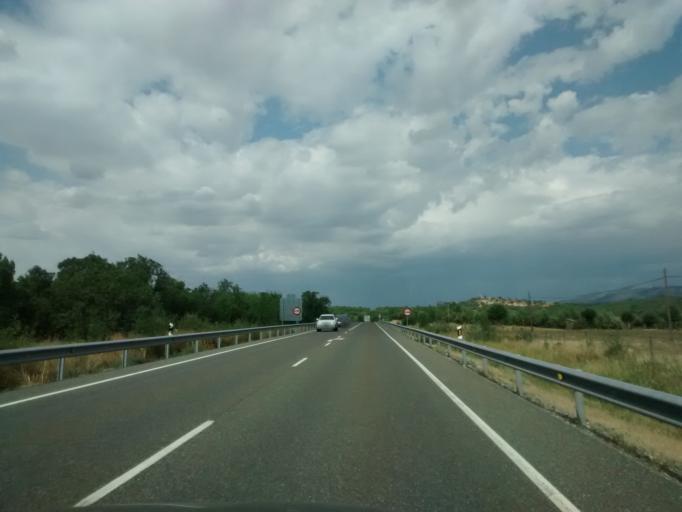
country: ES
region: Castille and Leon
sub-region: Provincia de Segovia
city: Navafria
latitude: 41.0723
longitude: -3.8101
